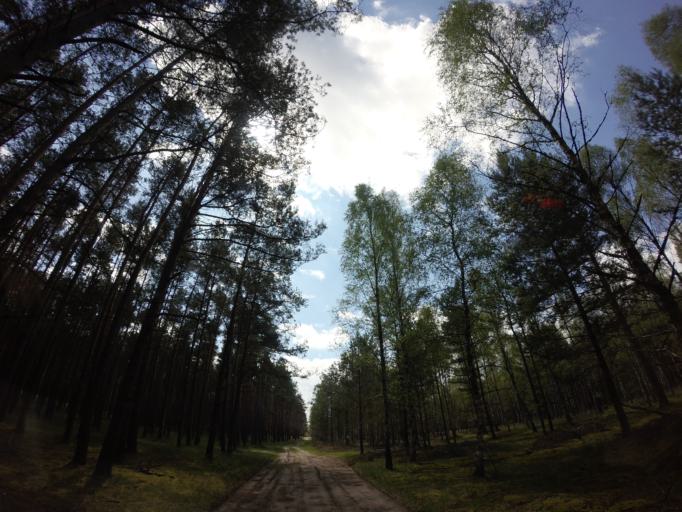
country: PL
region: West Pomeranian Voivodeship
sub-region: Powiat drawski
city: Kalisz Pomorski
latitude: 53.1972
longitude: 15.9350
